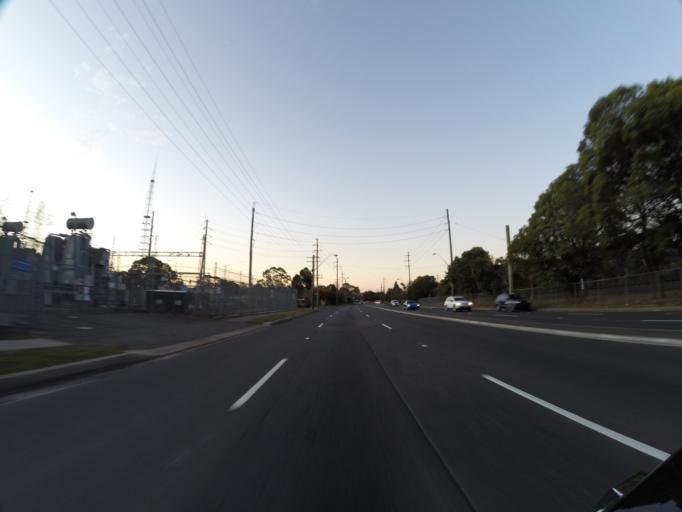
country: AU
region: New South Wales
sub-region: Sutherland Shire
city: Engadine
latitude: -34.0723
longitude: 151.0118
